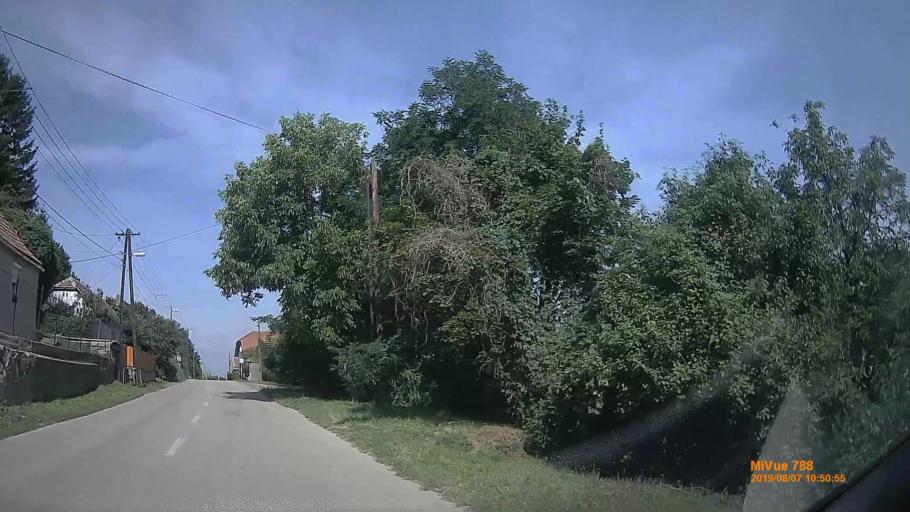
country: HU
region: Veszprem
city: Ajka
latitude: 47.0859
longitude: 17.5692
